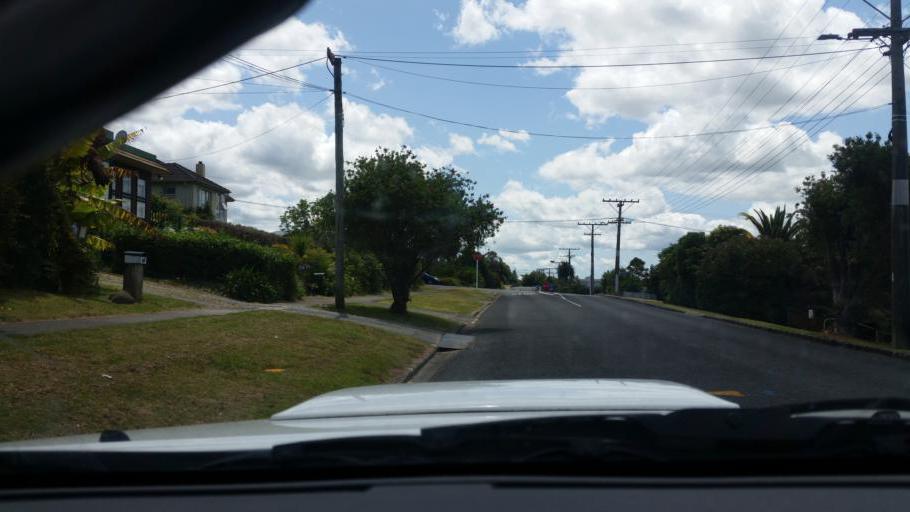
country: NZ
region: Northland
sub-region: Kaipara District
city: Dargaville
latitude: -35.9351
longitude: 173.8684
